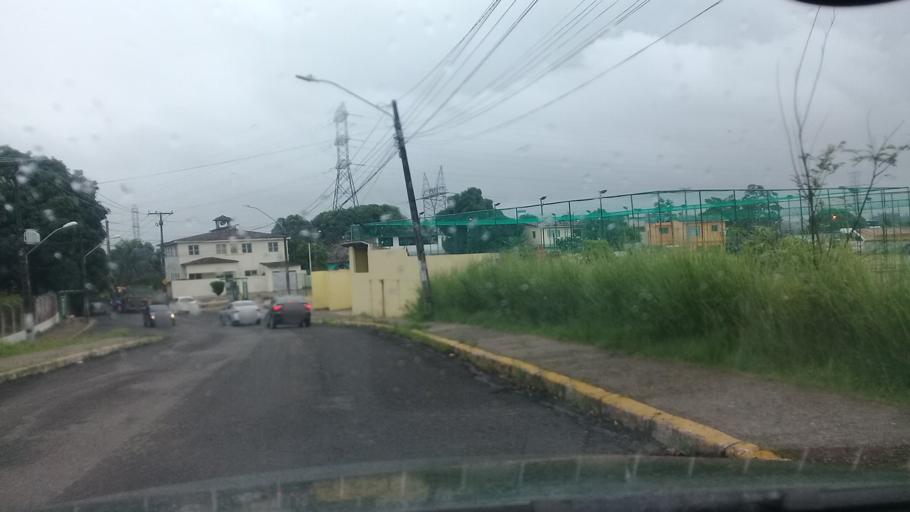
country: BR
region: Pernambuco
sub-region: Jaboatao Dos Guararapes
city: Jaboatao dos Guararapes
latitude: -8.0825
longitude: -34.9791
